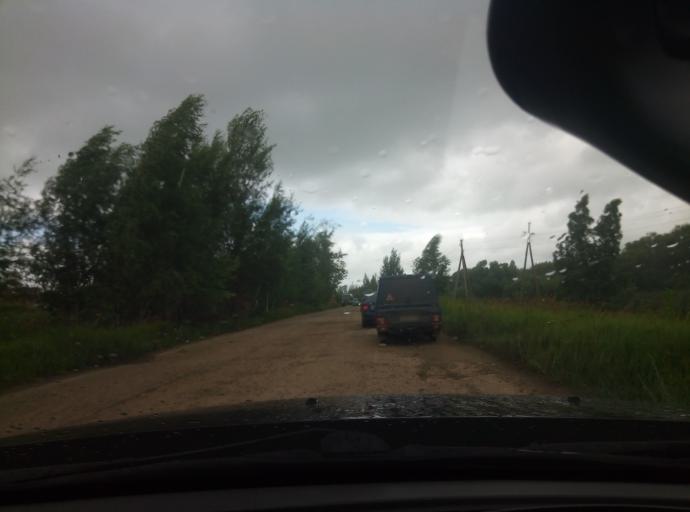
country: RU
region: Tula
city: Bolokhovo
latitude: 54.0773
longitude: 37.8199
